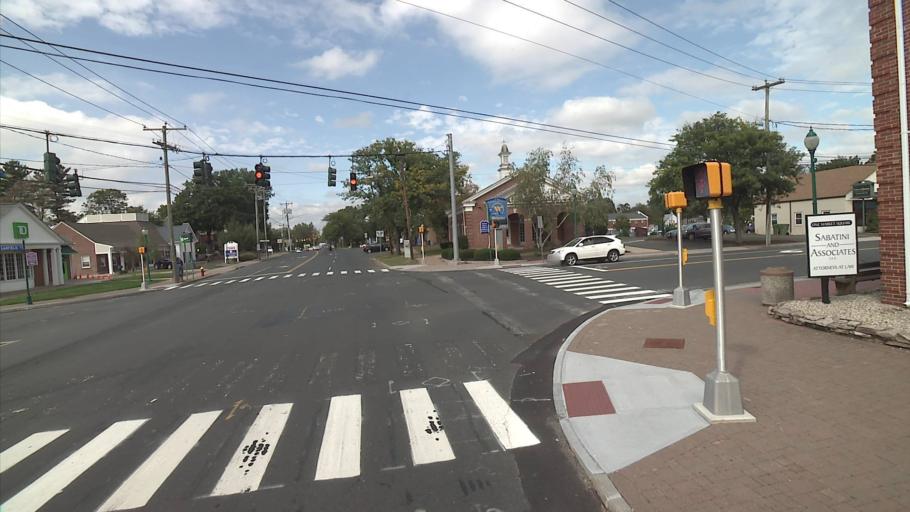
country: US
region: Connecticut
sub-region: Hartford County
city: Newington
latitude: 41.6961
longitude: -72.7229
